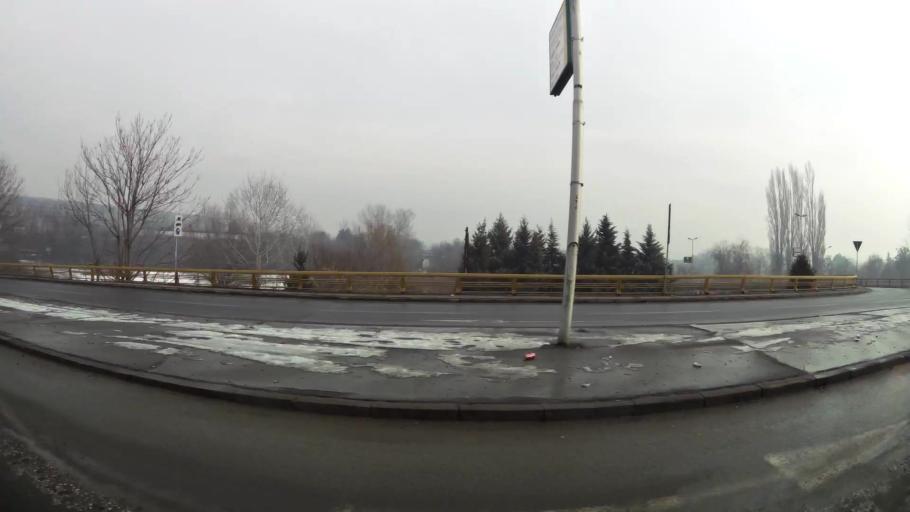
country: MK
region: Cair
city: Cair
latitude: 42.0033
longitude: 21.4705
